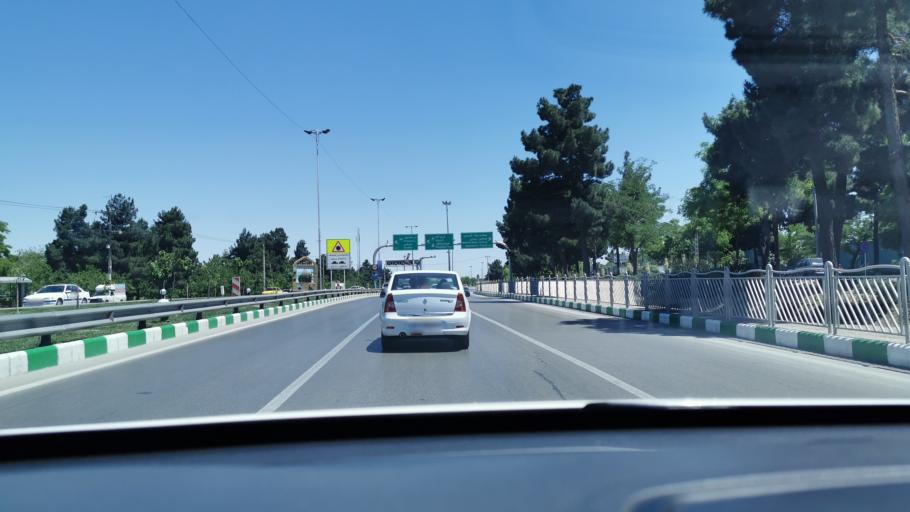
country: IR
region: Razavi Khorasan
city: Mashhad
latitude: 36.2536
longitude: 59.6037
